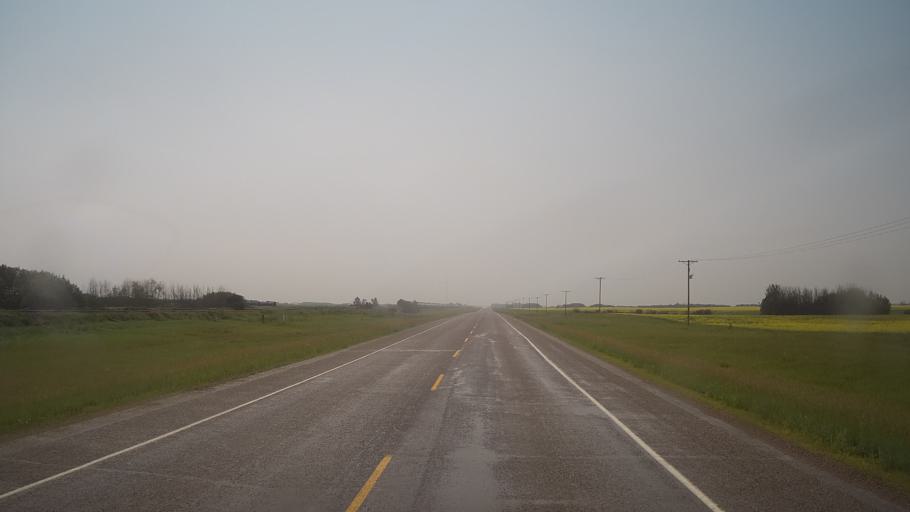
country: CA
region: Saskatchewan
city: Biggar
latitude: 52.1639
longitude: -108.2943
